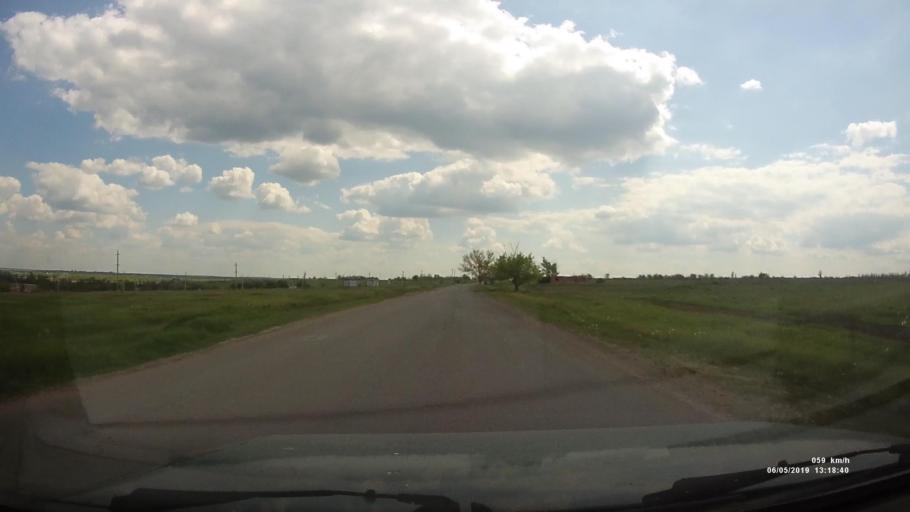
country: RU
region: Rostov
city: Ust'-Donetskiy
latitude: 47.7323
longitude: 40.9140
